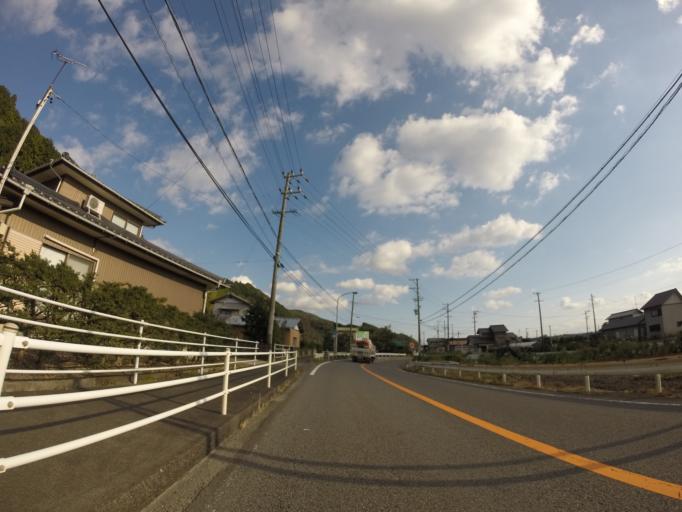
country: JP
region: Shizuoka
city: Kanaya
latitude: 34.8689
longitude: 138.1207
